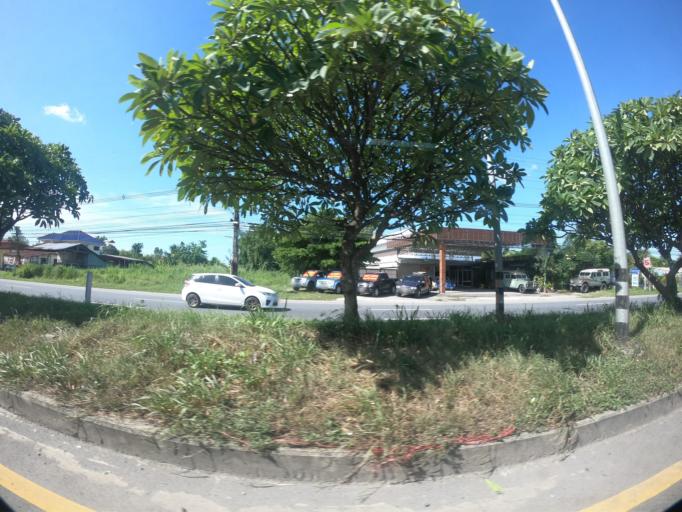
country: TH
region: Nakhon Nayok
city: Ban Na
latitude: 14.2561
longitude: 101.0829
